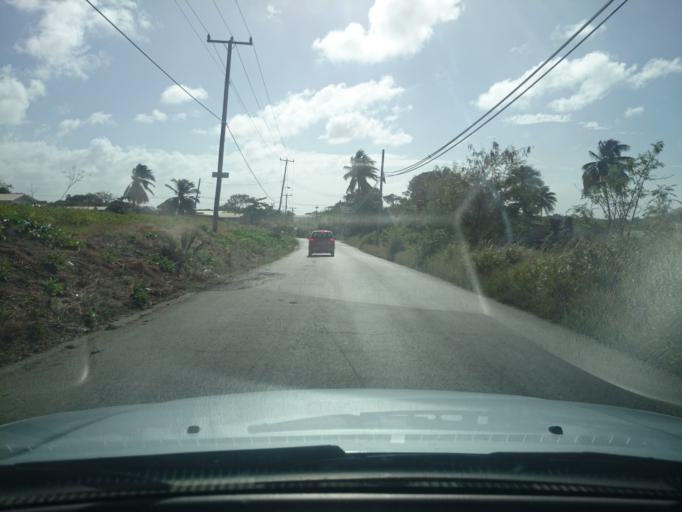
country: BB
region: Saint Lucy
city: Checker Hall
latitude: 13.2986
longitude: -59.6172
